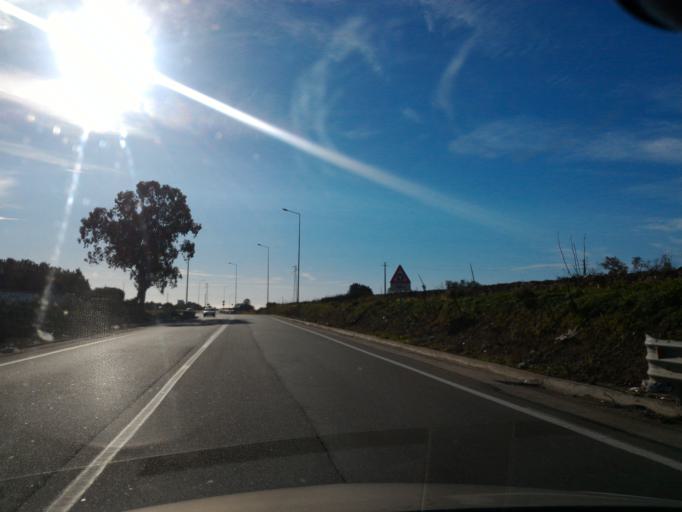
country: IT
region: Calabria
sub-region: Provincia di Crotone
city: Isola di Capo Rizzuto
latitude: 38.9707
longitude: 17.0800
